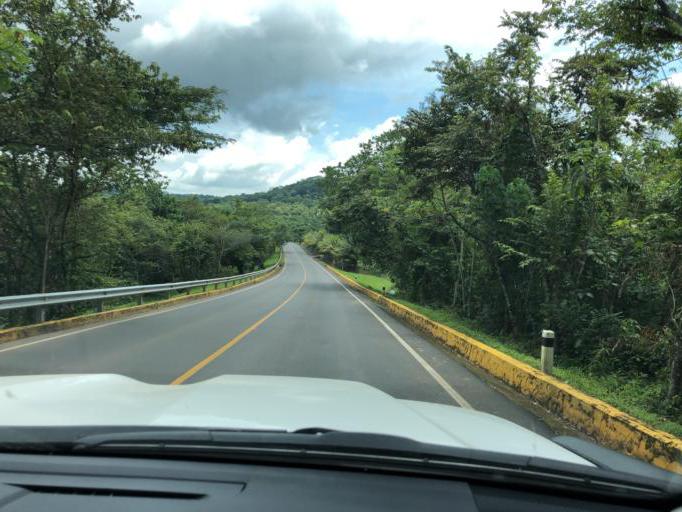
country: NI
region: Chontales
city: Villa Sandino
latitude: 12.0587
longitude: -85.0413
